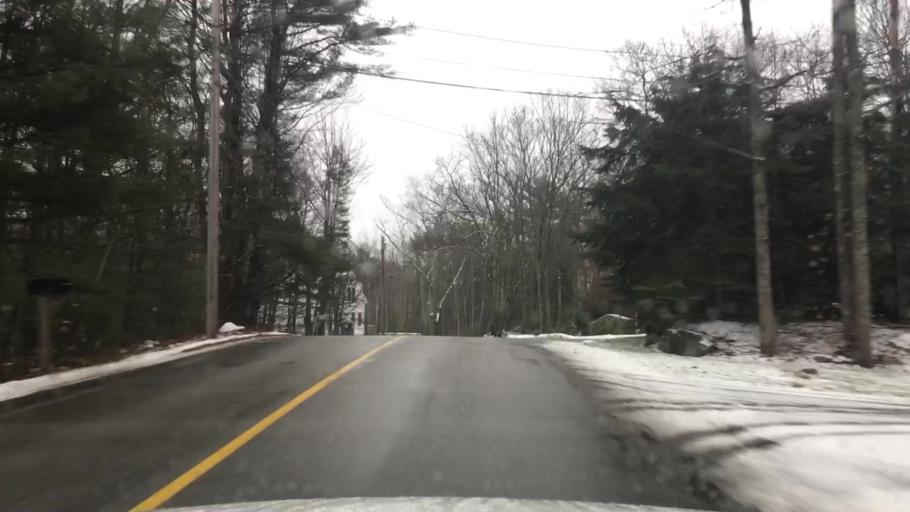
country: US
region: Maine
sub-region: York County
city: Kennebunkport
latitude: 43.3732
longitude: -70.4546
